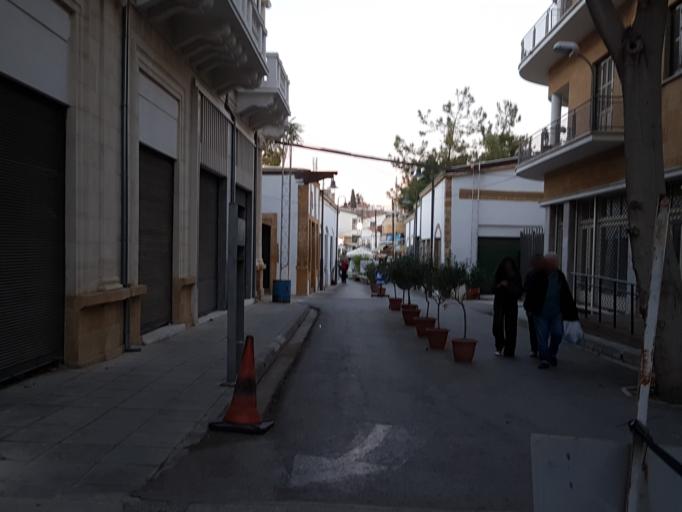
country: CY
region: Lefkosia
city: Nicosia
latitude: 35.1746
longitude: 33.3614
